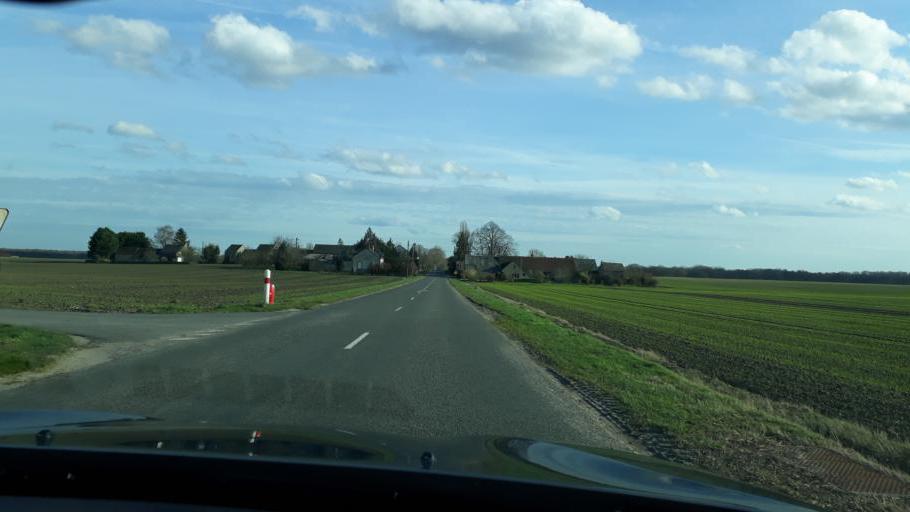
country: FR
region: Centre
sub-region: Departement du Loiret
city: Chilleurs-aux-Bois
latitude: 48.0686
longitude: 2.1429
